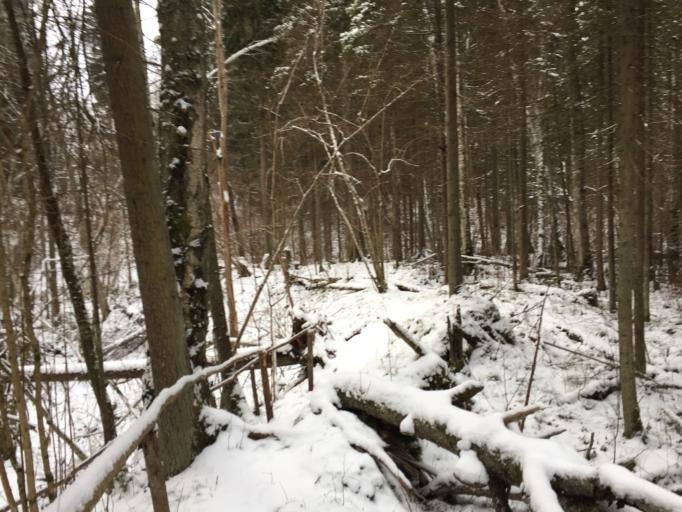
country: LV
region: Amatas Novads
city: Drabesi
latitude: 57.2202
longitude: 25.1667
